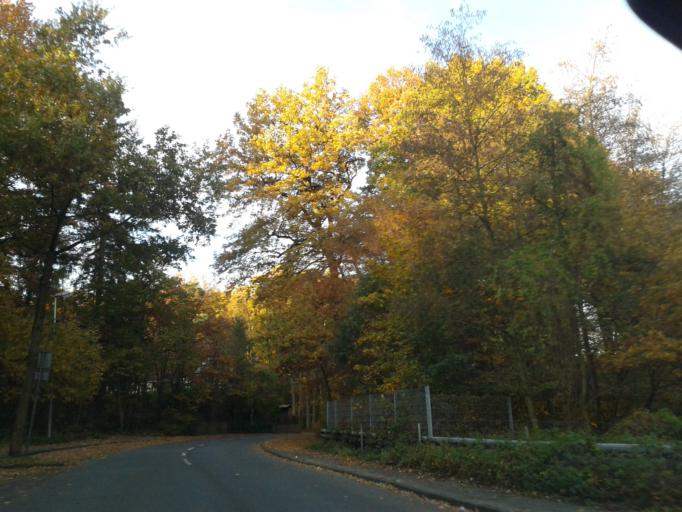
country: DE
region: North Rhine-Westphalia
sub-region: Regierungsbezirk Detmold
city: Paderborn
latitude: 51.7554
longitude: 8.7164
